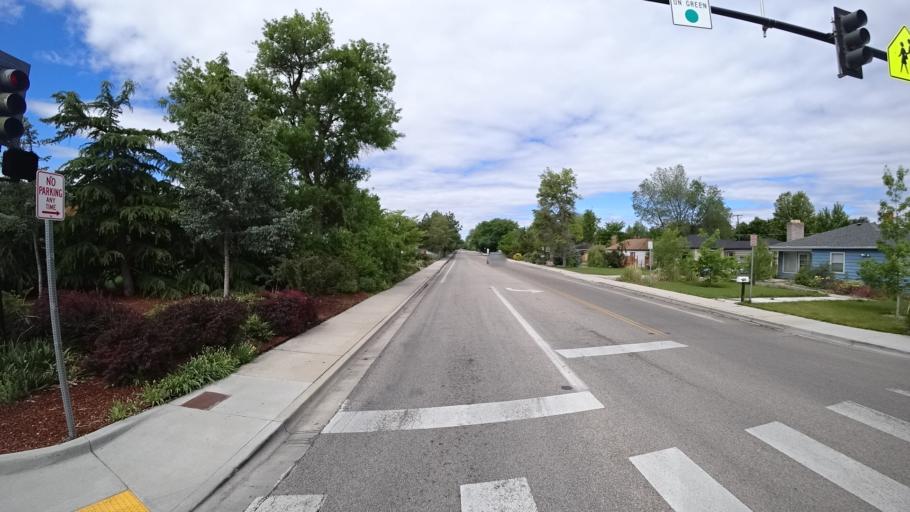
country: US
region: Idaho
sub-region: Ada County
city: Boise
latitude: 43.5789
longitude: -116.1837
